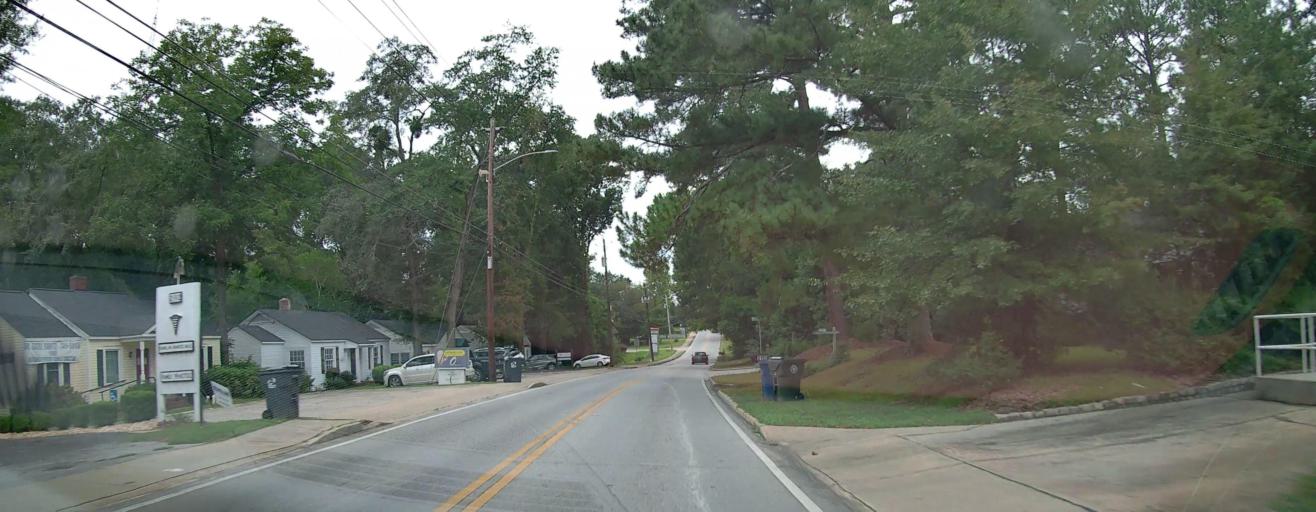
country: US
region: Georgia
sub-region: Bibb County
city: Macon
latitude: 32.8538
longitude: -83.6511
